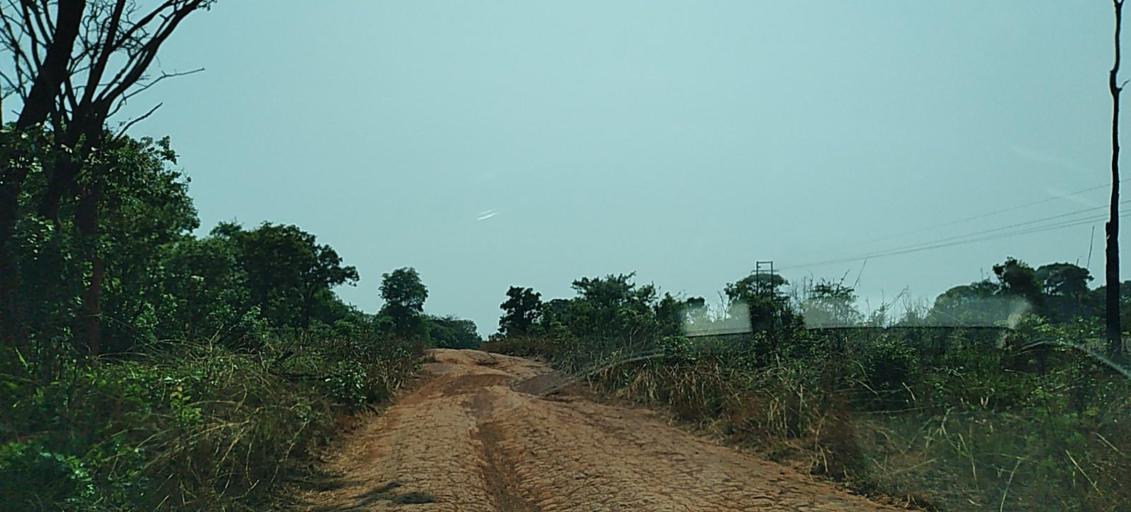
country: ZM
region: North-Western
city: Kansanshi
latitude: -12.0095
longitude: 26.5110
